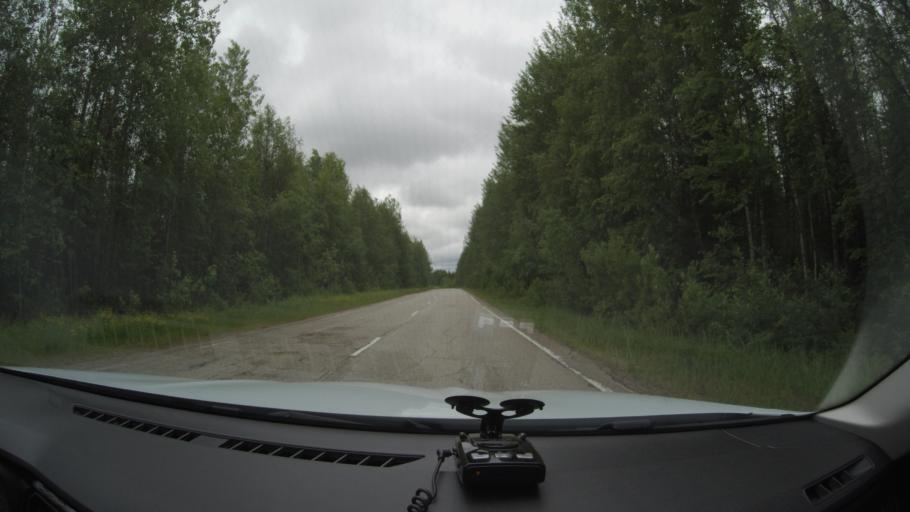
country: RU
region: Komi Republic
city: Nizhniy Odes
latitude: 63.6213
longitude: 54.6090
